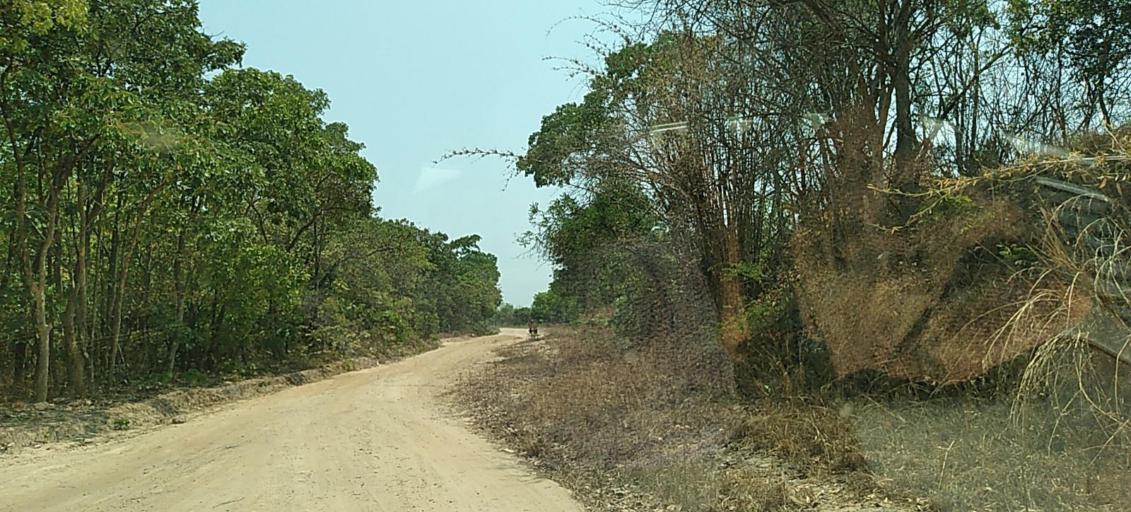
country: ZM
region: Copperbelt
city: Kalulushi
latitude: -12.9472
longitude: 28.1519
